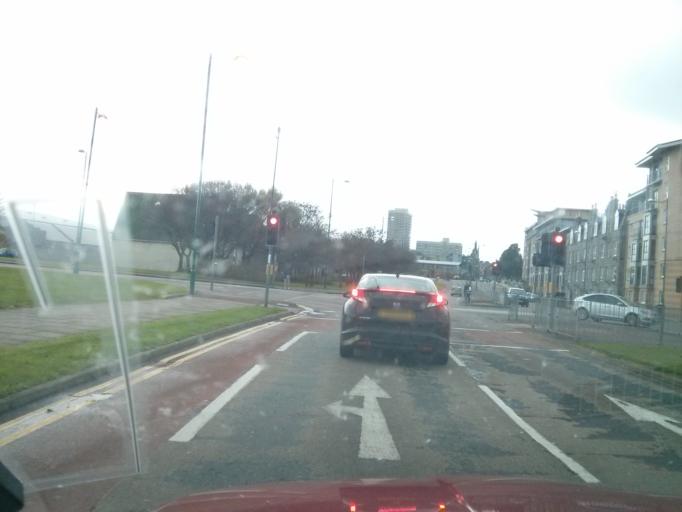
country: GB
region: Scotland
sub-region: Aberdeen City
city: Aberdeen
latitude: 57.1520
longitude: -2.0823
